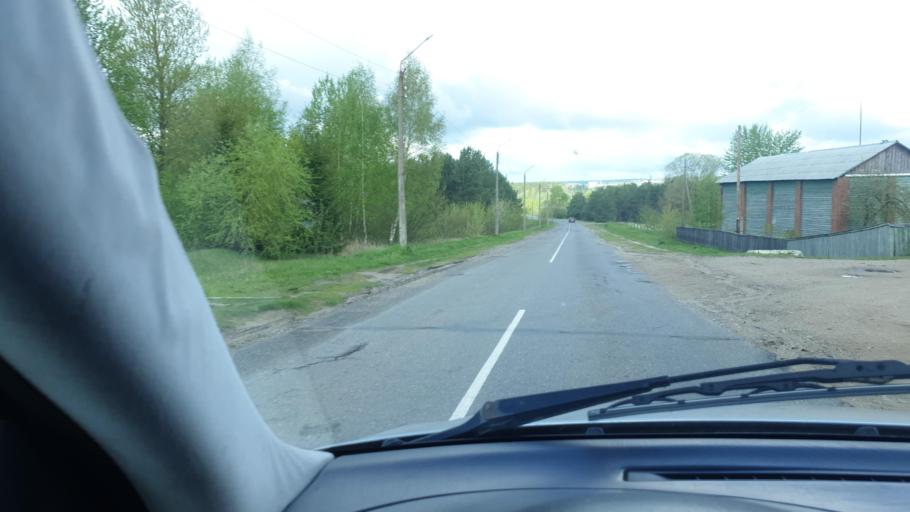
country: BY
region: Vitebsk
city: Lyepyel'
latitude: 54.8760
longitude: 28.6740
